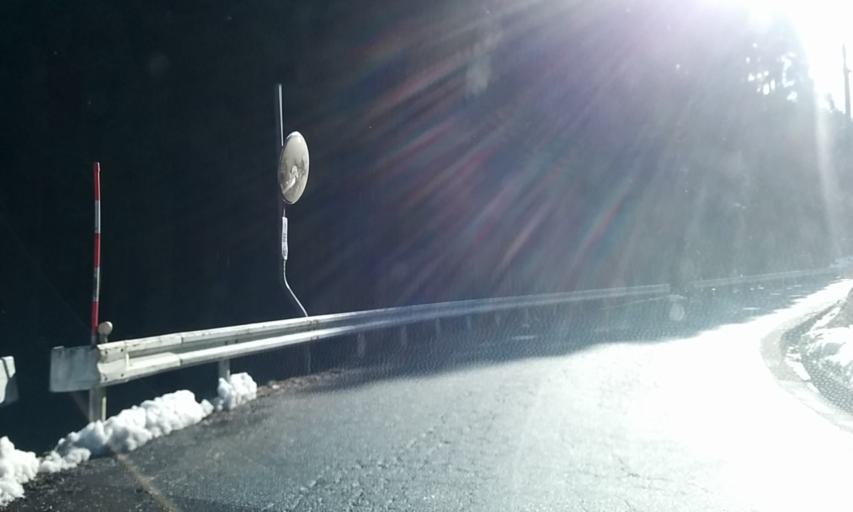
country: JP
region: Hyogo
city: Toyooka
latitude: 35.4178
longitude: 134.9628
